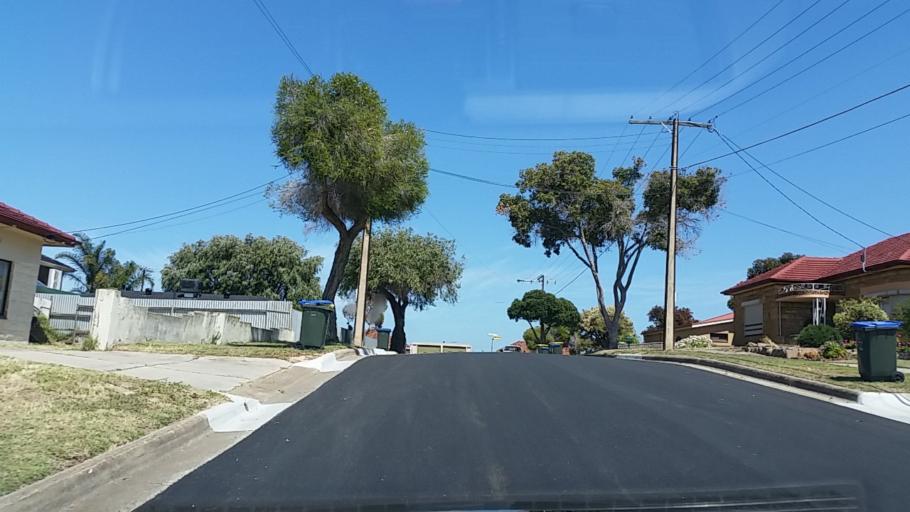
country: AU
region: South Australia
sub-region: Charles Sturt
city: Seaton
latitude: -34.9027
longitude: 138.5248
